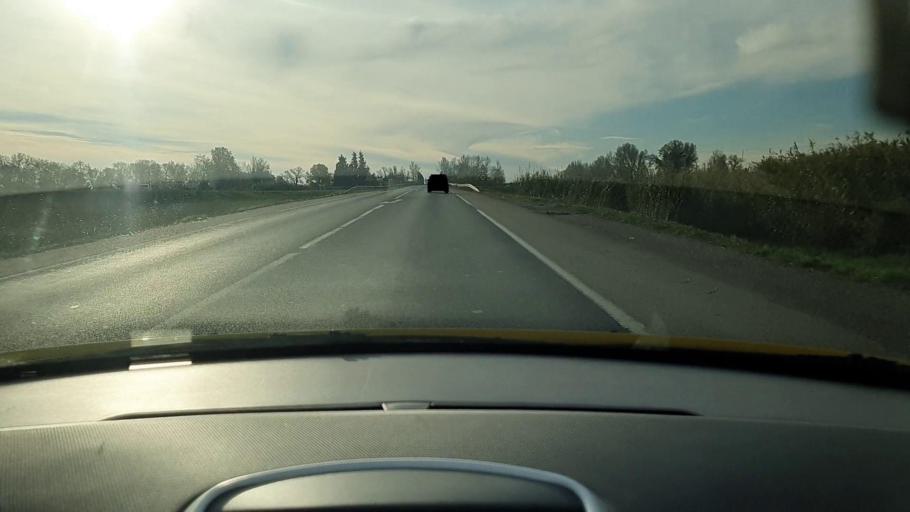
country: FR
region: Languedoc-Roussillon
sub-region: Departement du Gard
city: Fourques
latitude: 43.6898
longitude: 4.6049
